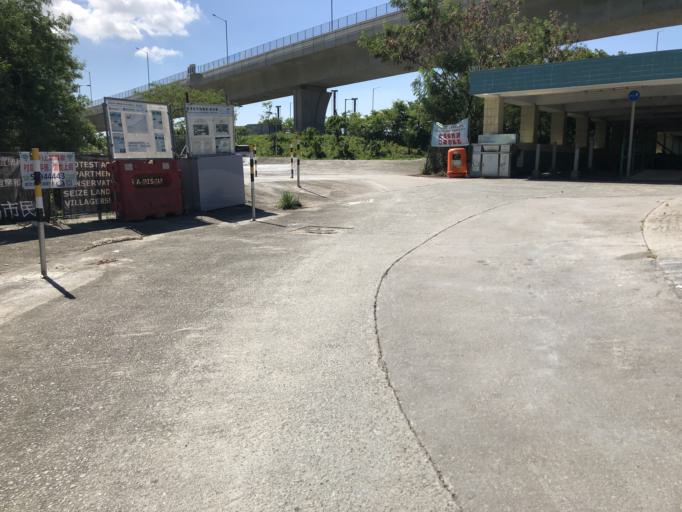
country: HK
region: Tuen Mun
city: Tuen Mun
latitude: 22.2979
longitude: 113.9678
